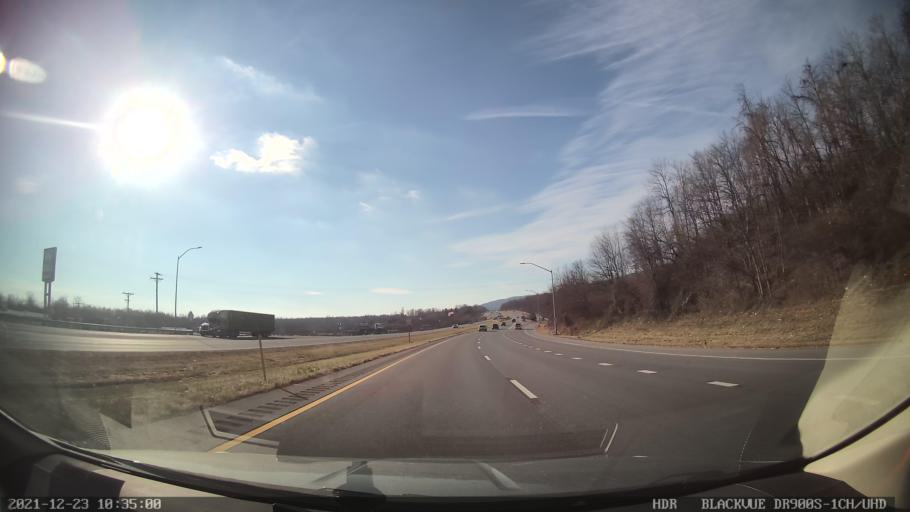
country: US
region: Maryland
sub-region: Frederick County
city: Thurmont
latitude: 39.6170
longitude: -77.4186
